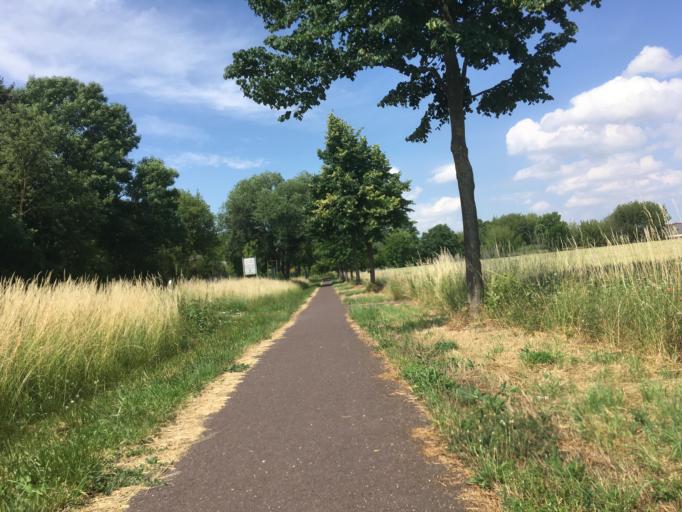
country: DE
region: Saxony-Anhalt
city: Osternienburg
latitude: 51.7527
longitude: 12.0148
